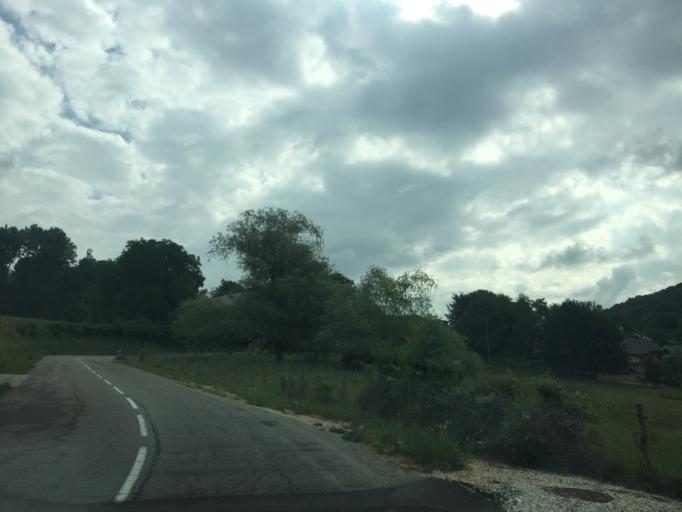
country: FR
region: Rhone-Alpes
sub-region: Departement de la Savoie
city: Barby
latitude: 45.5772
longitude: 5.9835
